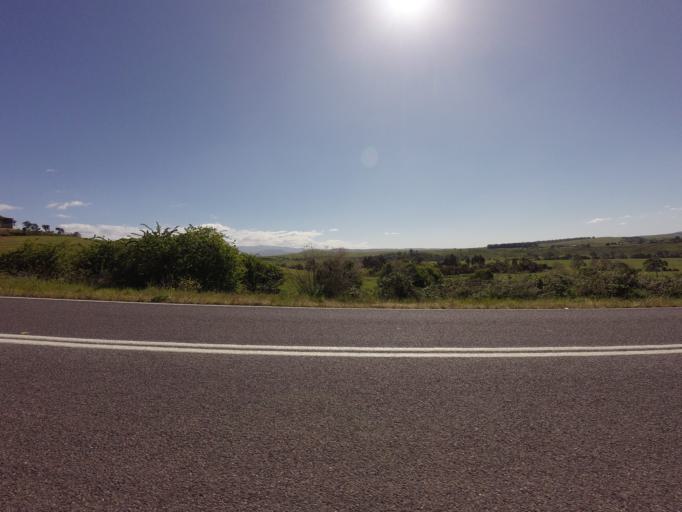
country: AU
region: Tasmania
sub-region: Derwent Valley
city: New Norfolk
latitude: -42.6941
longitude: 146.9392
